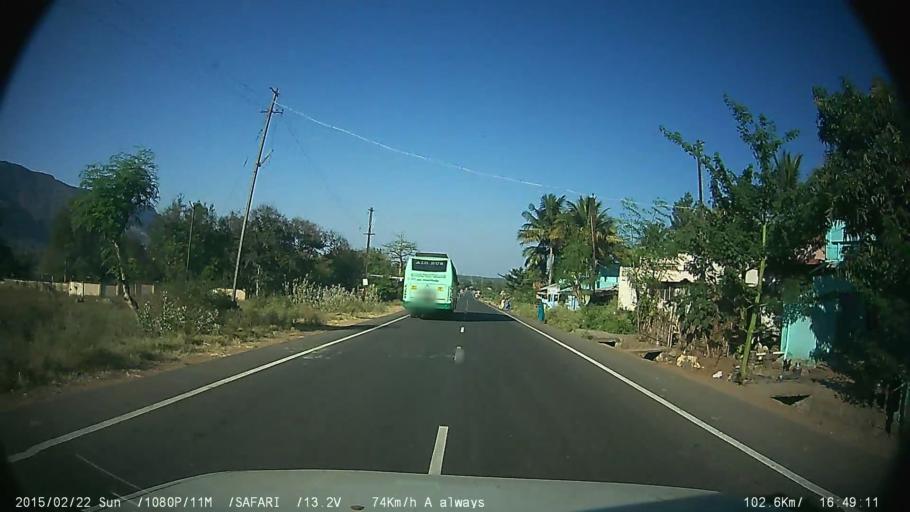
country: IN
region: Tamil Nadu
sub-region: Theni
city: Gudalur
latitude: 9.6302
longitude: 77.1997
